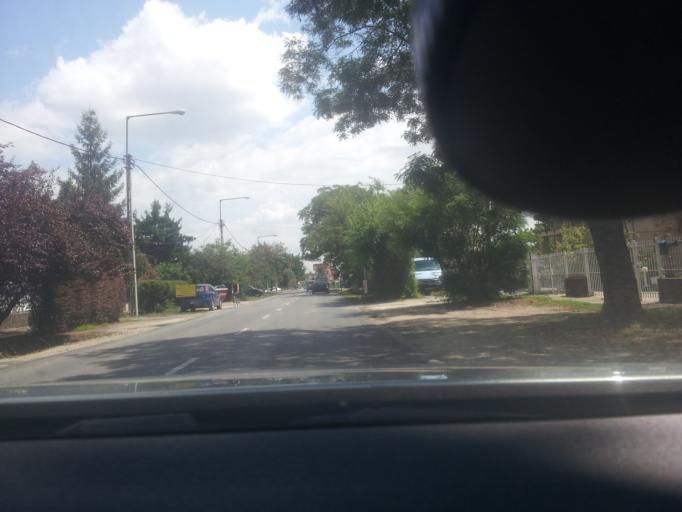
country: HU
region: Budapest
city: Budapest XVIII. keruelet
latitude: 47.4339
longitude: 19.1974
